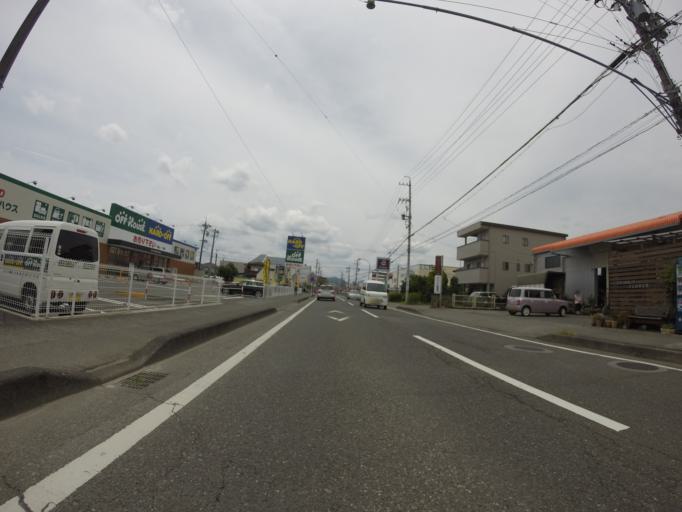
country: JP
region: Shizuoka
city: Shizuoka-shi
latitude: 35.0064
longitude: 138.4101
